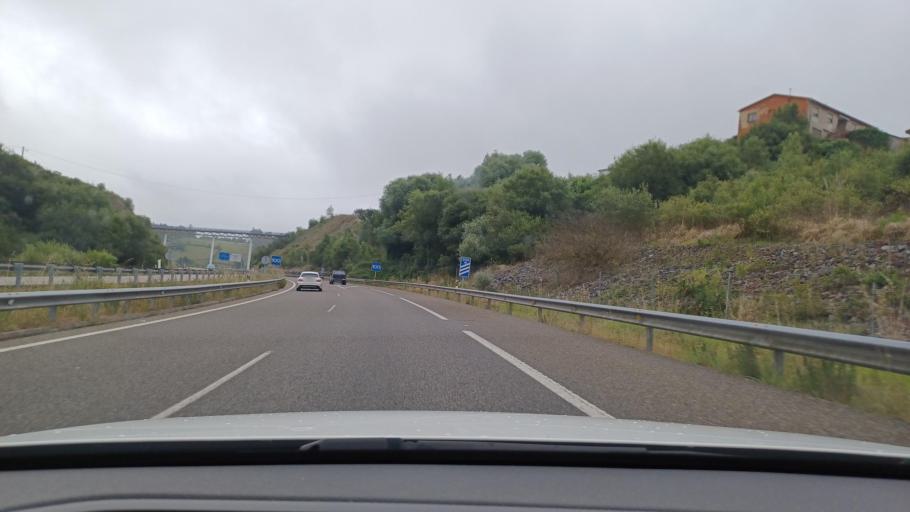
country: ES
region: Asturias
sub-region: Province of Asturias
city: Lugones
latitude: 43.4518
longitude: -5.7705
